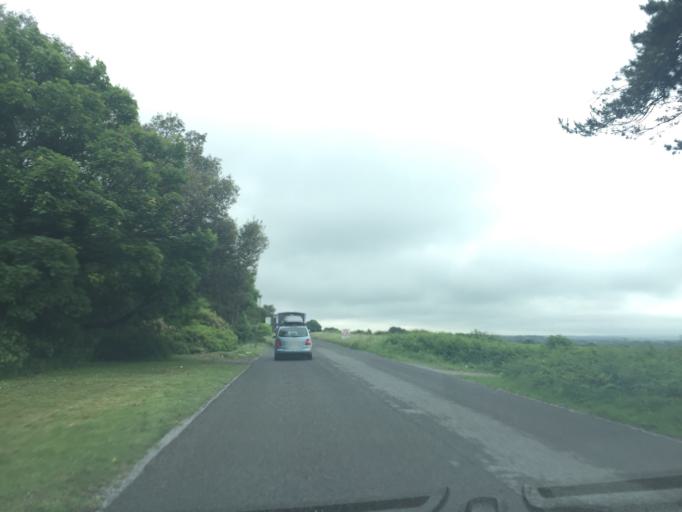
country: GB
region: England
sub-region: Dorset
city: Wareham
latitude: 50.6822
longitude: -2.1405
